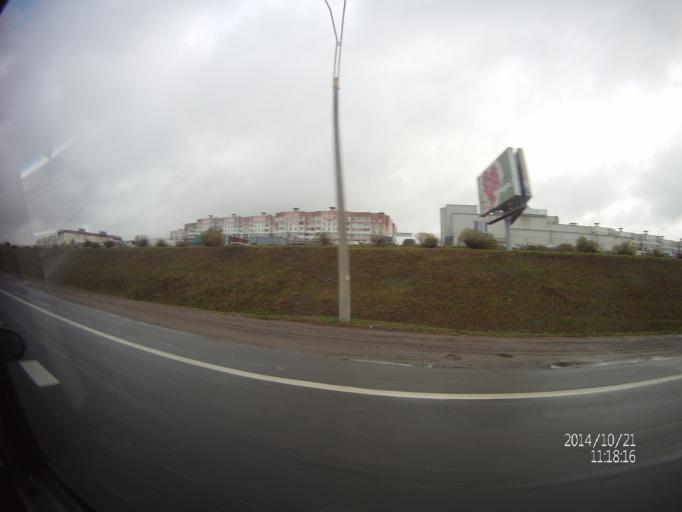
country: BY
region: Minsk
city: Malinovka
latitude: 53.8827
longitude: 27.4164
